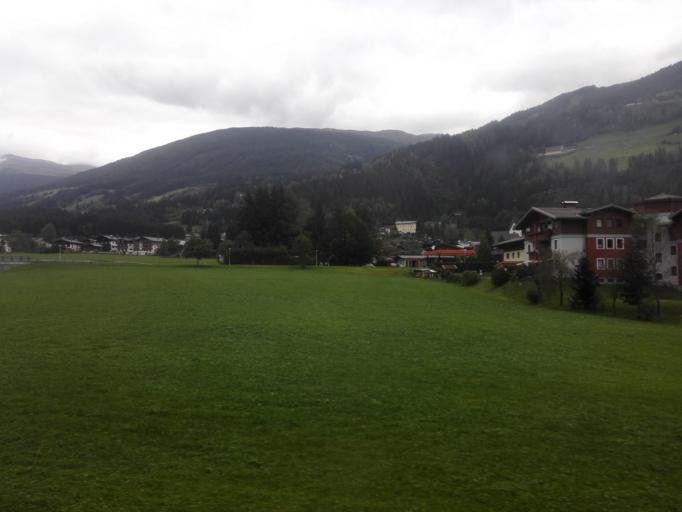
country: AT
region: Salzburg
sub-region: Politischer Bezirk Zell am See
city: Neukirchen am Grossvenediger
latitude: 47.2505
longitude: 12.2799
